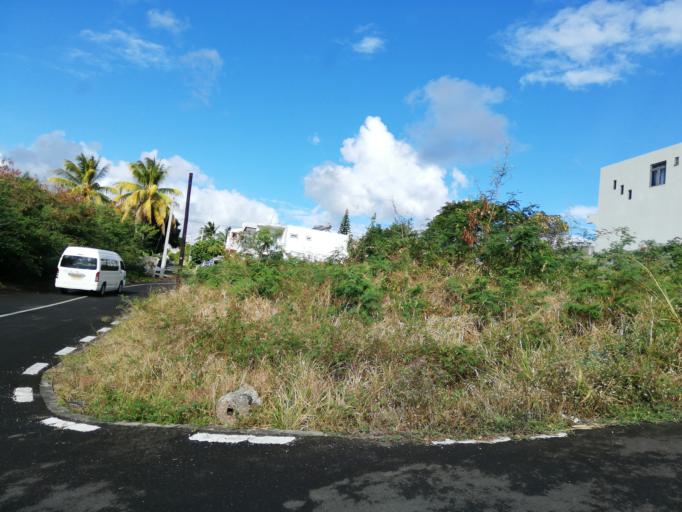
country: MU
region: Black River
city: Petite Riviere
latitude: -20.2021
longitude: 57.4639
